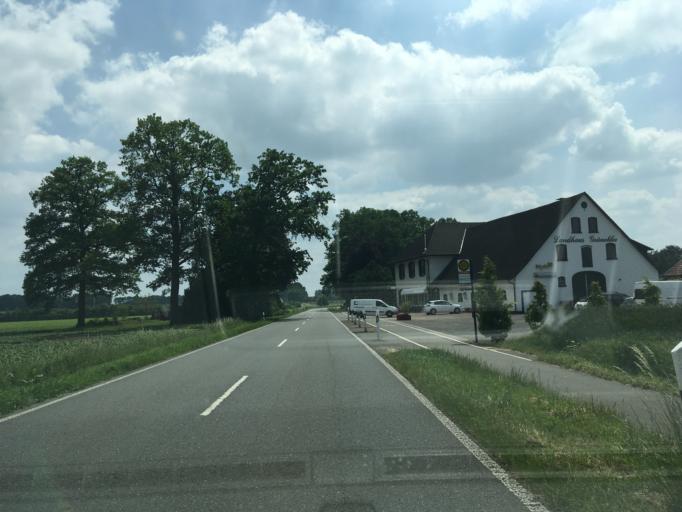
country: DE
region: North Rhine-Westphalia
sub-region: Regierungsbezirk Munster
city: Borken
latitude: 51.8268
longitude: 6.7797
